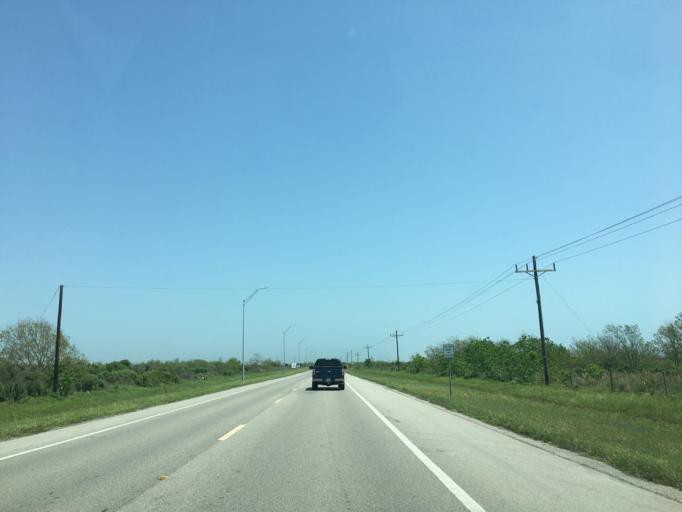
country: US
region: Texas
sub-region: Galveston County
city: Galveston
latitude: 29.3886
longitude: -94.7354
